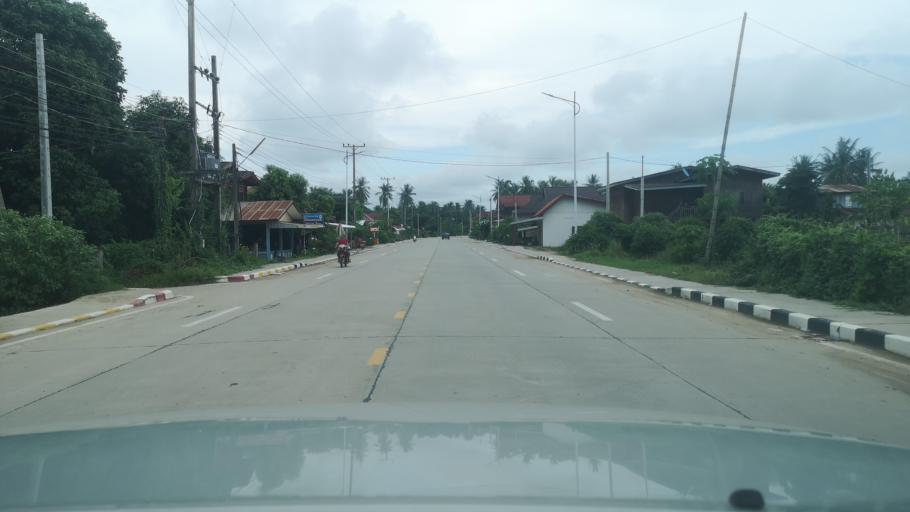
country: TH
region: Nong Khai
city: Tha Bo
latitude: 17.8263
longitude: 102.6556
